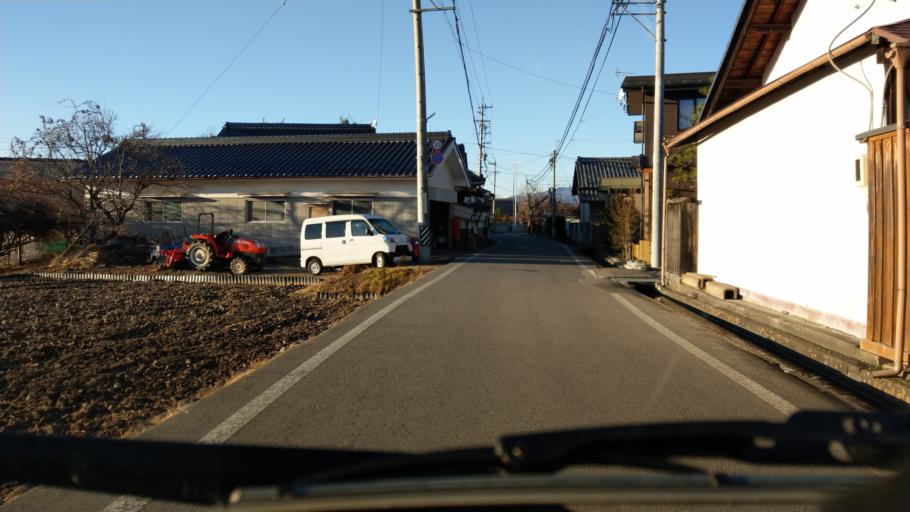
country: JP
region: Nagano
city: Saku
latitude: 36.2389
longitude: 138.4709
